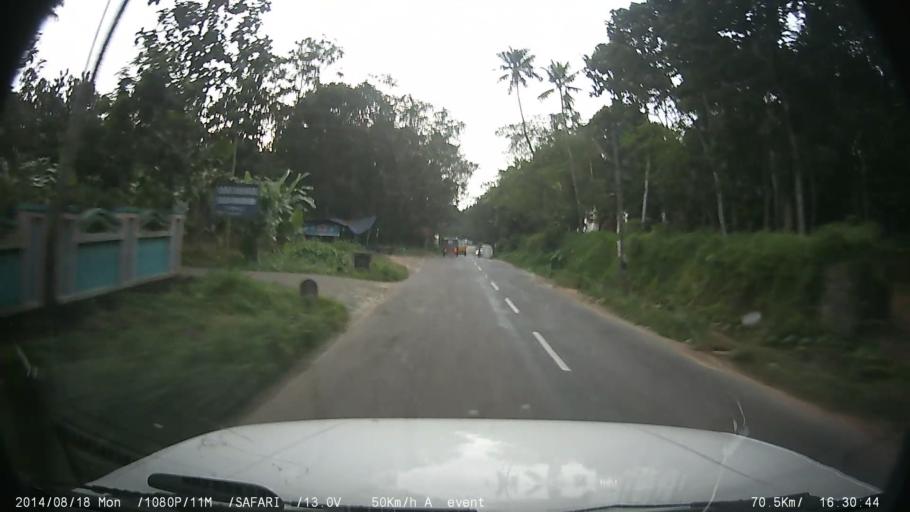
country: IN
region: Kerala
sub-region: Kottayam
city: Palackattumala
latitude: 9.7927
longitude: 76.5754
